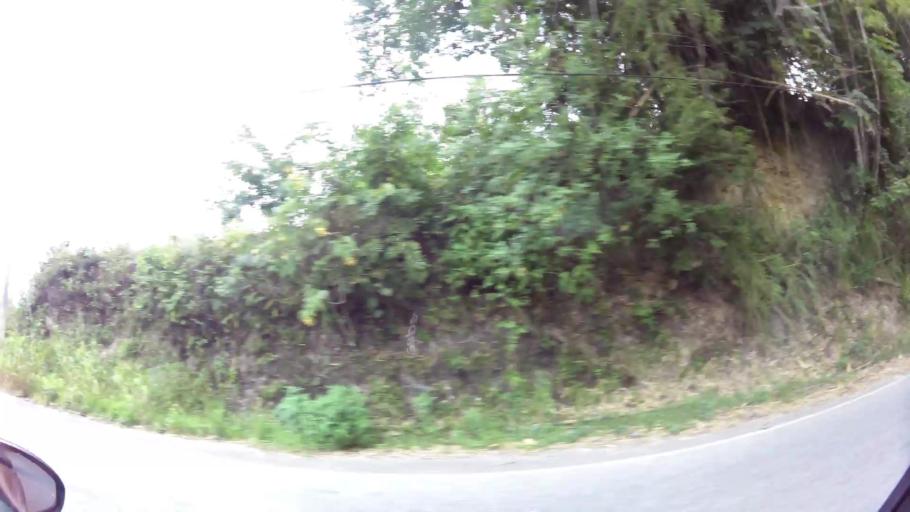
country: TT
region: Diego Martin
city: Petit Valley
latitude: 10.7604
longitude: -61.4447
